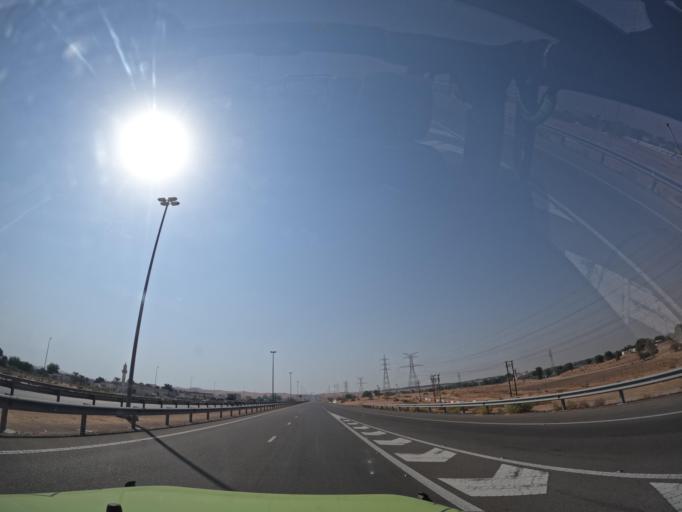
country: OM
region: Al Buraimi
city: Al Buraymi
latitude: 24.3633
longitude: 55.7302
